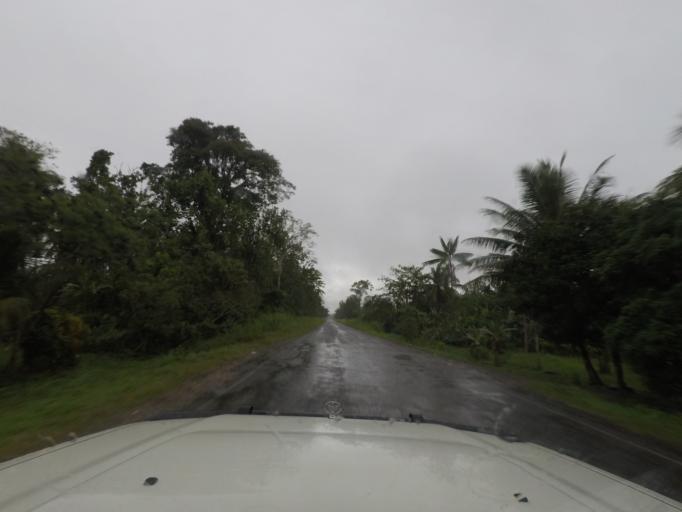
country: PG
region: Madang
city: Madang
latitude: -5.3885
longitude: 145.6860
